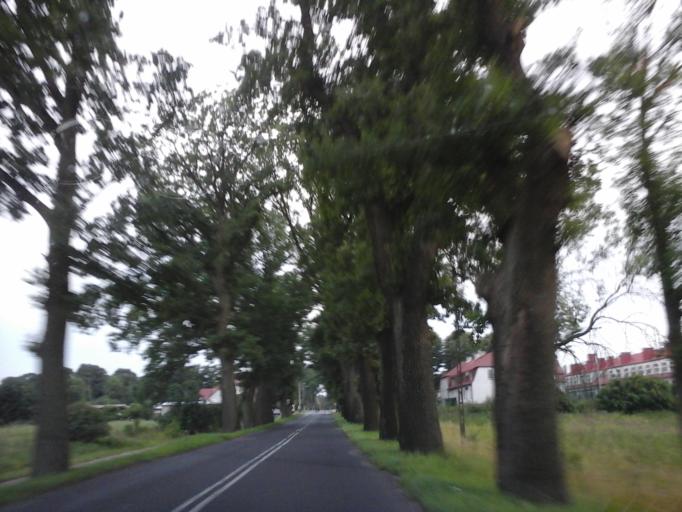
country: PL
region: West Pomeranian Voivodeship
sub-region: Powiat goleniowski
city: Maszewo
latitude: 53.5389
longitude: 15.1222
